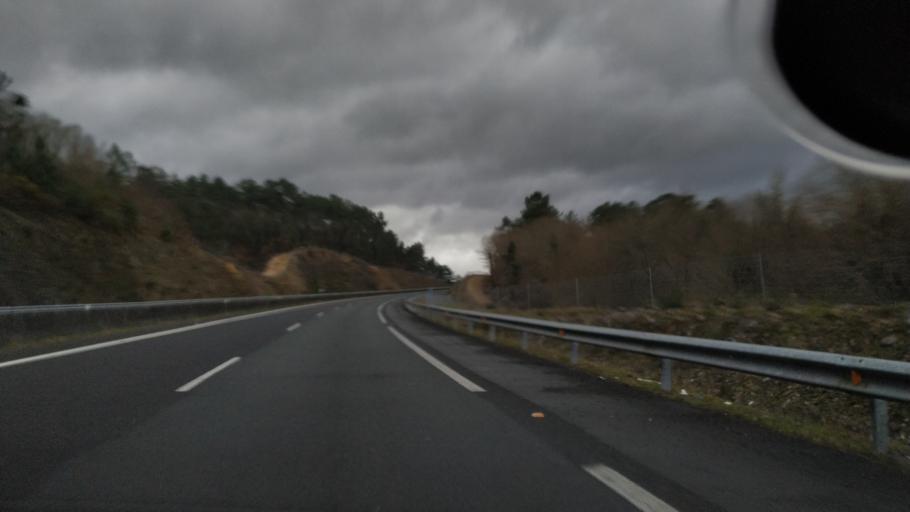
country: ES
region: Galicia
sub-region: Provincia da Coruna
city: Vedra
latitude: 42.7959
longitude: -8.4833
